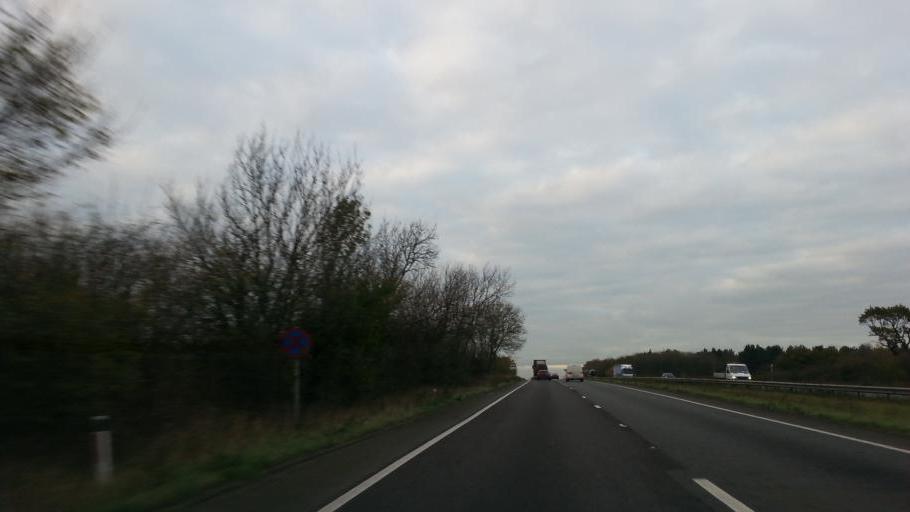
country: GB
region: England
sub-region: District of Rutland
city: Greetham
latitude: 52.7479
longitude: -0.6049
